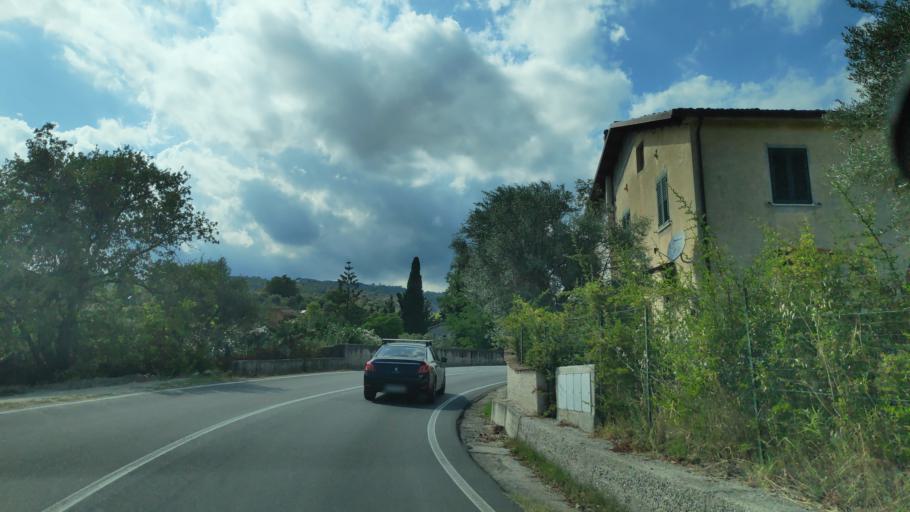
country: IT
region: Calabria
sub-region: Provincia di Catanzaro
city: Santa Caterina dello Ionio Marina
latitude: 38.5277
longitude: 16.5541
